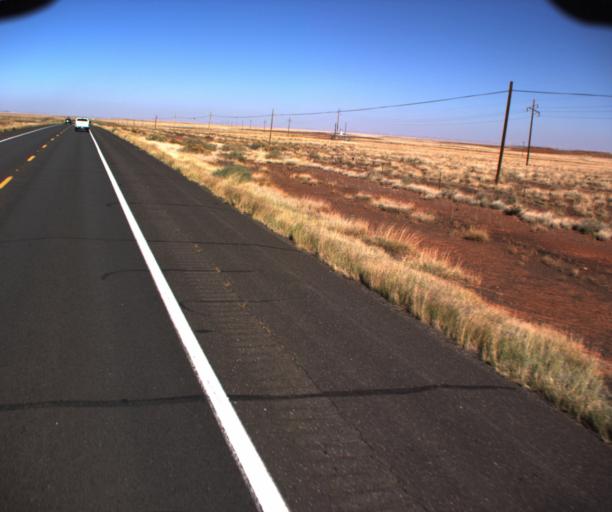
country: US
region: Arizona
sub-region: Coconino County
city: Flagstaff
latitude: 35.6645
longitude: -111.5120
